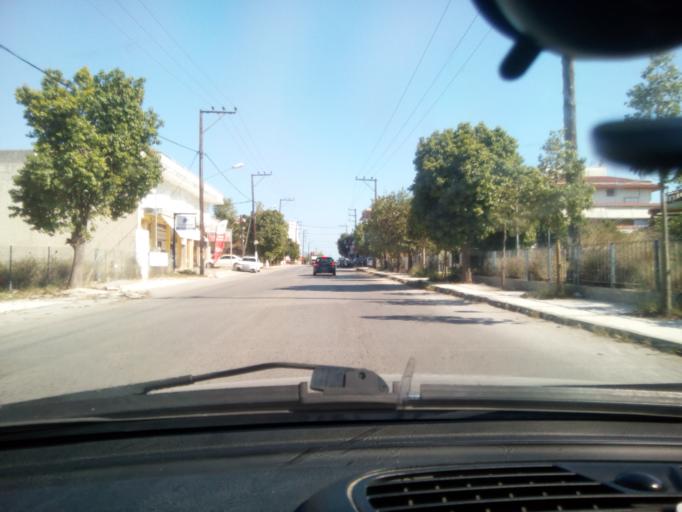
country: GR
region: Central Greece
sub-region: Nomos Evvoias
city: Vasilikon
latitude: 38.4229
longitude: 23.6764
